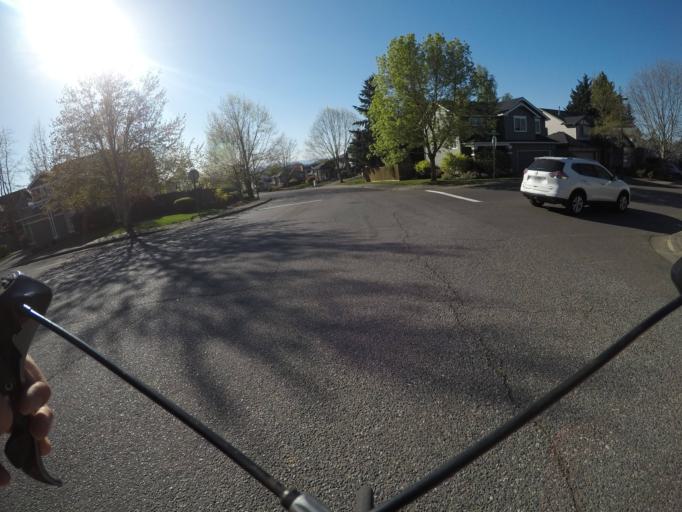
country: US
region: Oregon
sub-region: Washington County
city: King City
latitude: 45.4193
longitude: -122.8420
